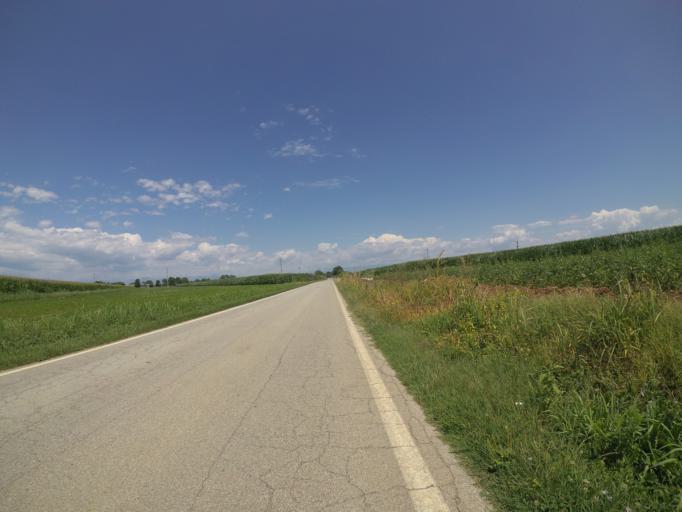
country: IT
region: Friuli Venezia Giulia
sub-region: Provincia di Udine
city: Bertiolo
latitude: 45.9434
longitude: 13.0734
